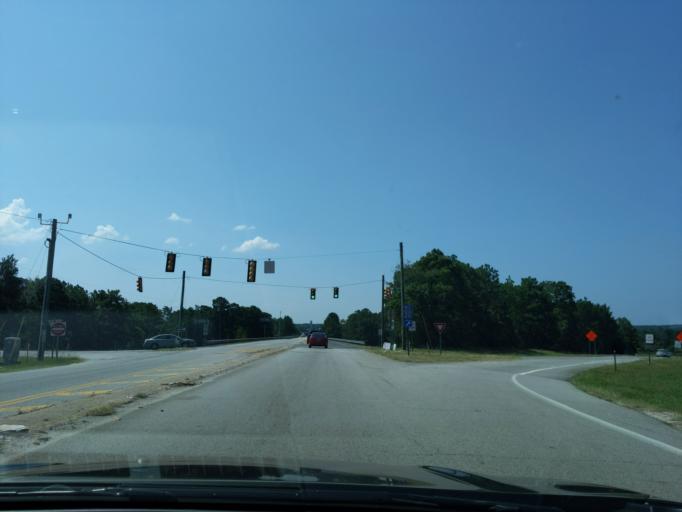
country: US
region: South Carolina
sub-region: Lexington County
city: Red Bank
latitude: 33.9290
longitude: -81.2905
